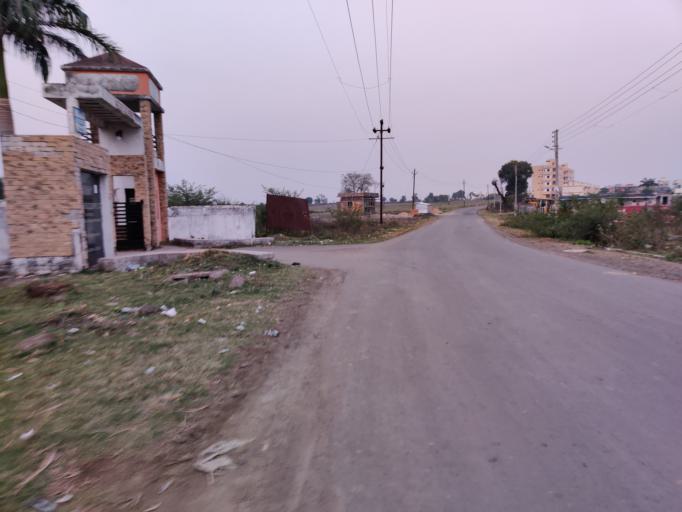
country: IN
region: Maharashtra
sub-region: Nagpur Division
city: Kamthi
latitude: 21.1956
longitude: 79.1488
